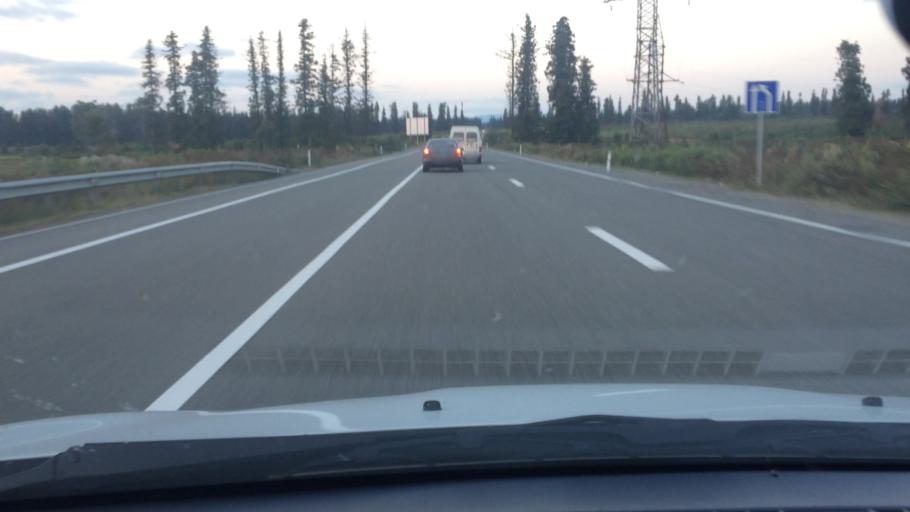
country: GE
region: Ajaria
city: Ochkhamuri
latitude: 41.8340
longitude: 41.8229
